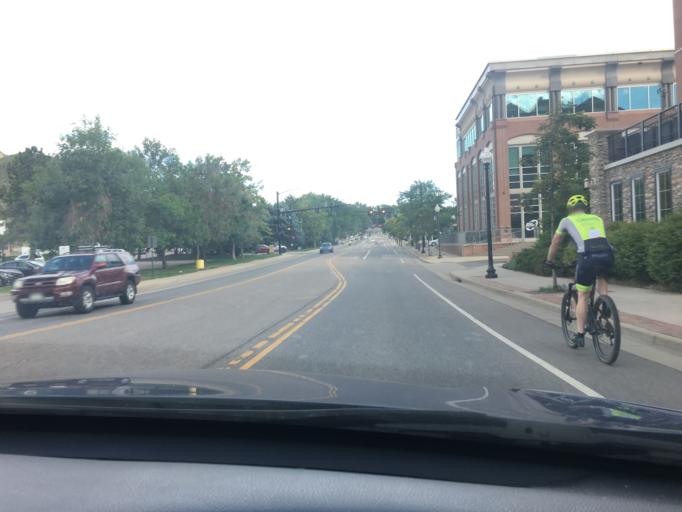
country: US
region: Colorado
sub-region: Jefferson County
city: Golden
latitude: 39.7573
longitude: -105.2199
